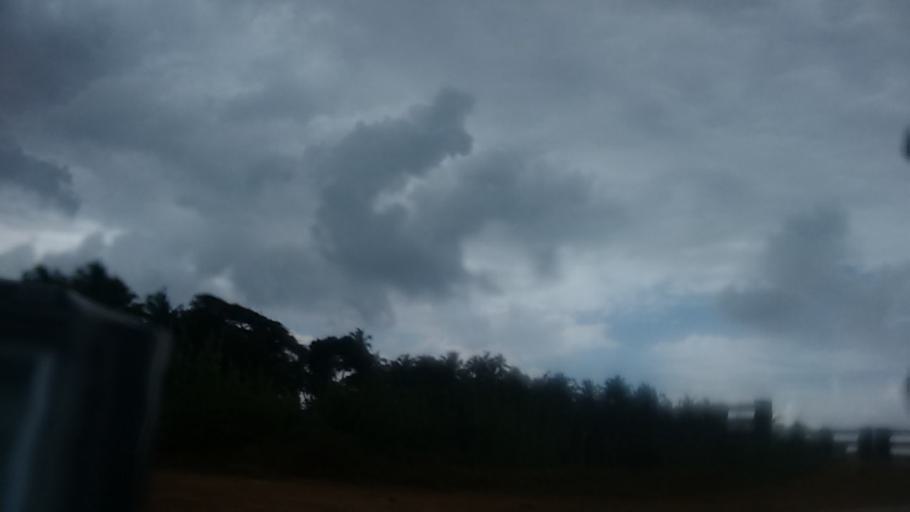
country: IN
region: Kerala
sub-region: Thrissur District
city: Trichur
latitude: 10.5277
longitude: 76.1666
